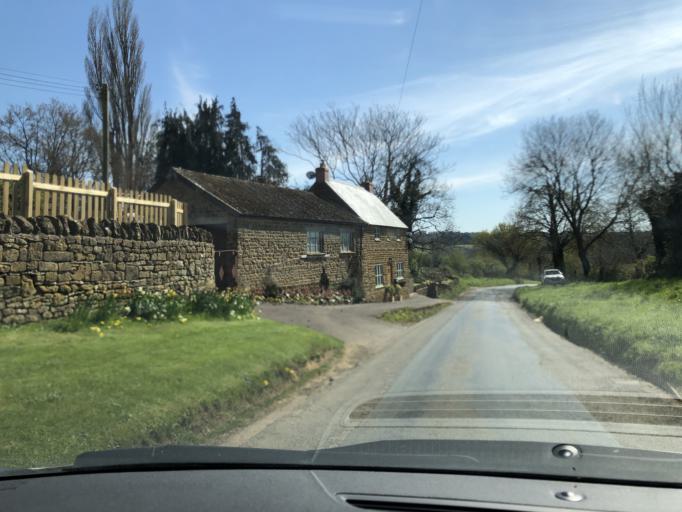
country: GB
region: England
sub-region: Oxfordshire
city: Hook Norton
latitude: 51.9977
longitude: -1.4374
